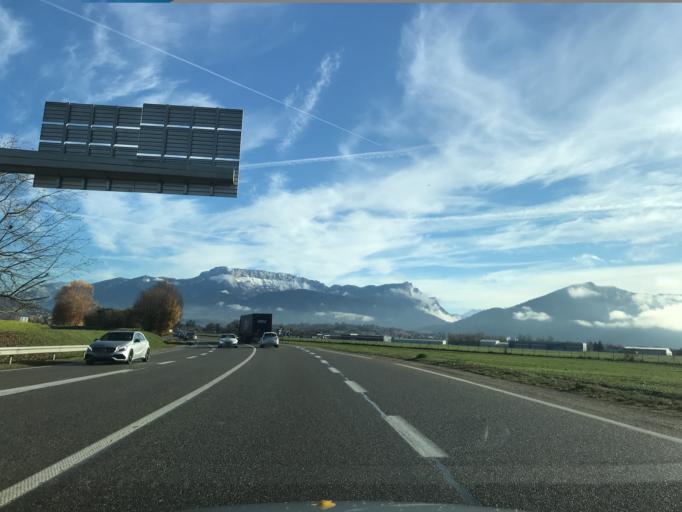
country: FR
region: Rhone-Alpes
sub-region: Departement de la Haute-Savoie
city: Epagny
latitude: 45.9301
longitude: 6.0939
